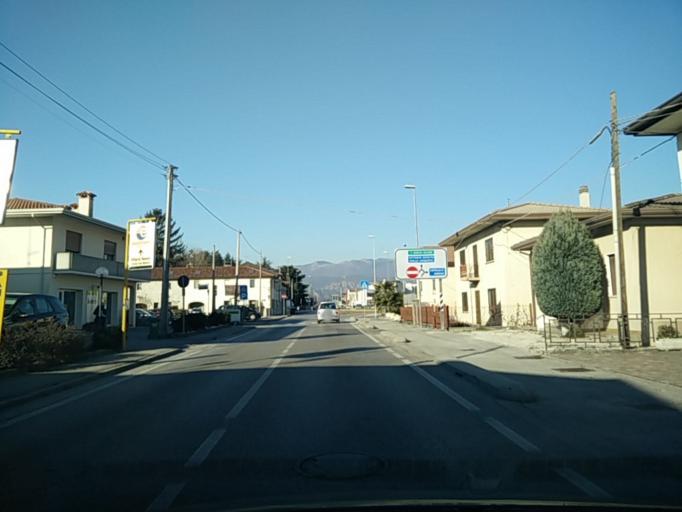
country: IT
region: Veneto
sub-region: Provincia di Treviso
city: Cappella Maggiore
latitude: 45.9568
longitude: 12.3603
